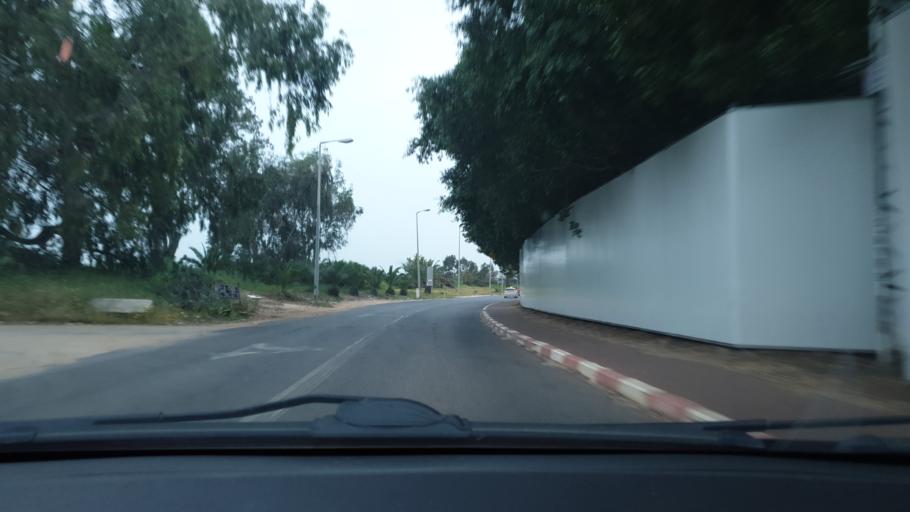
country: IL
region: Central District
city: Kefar Habad
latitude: 31.9863
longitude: 34.8432
